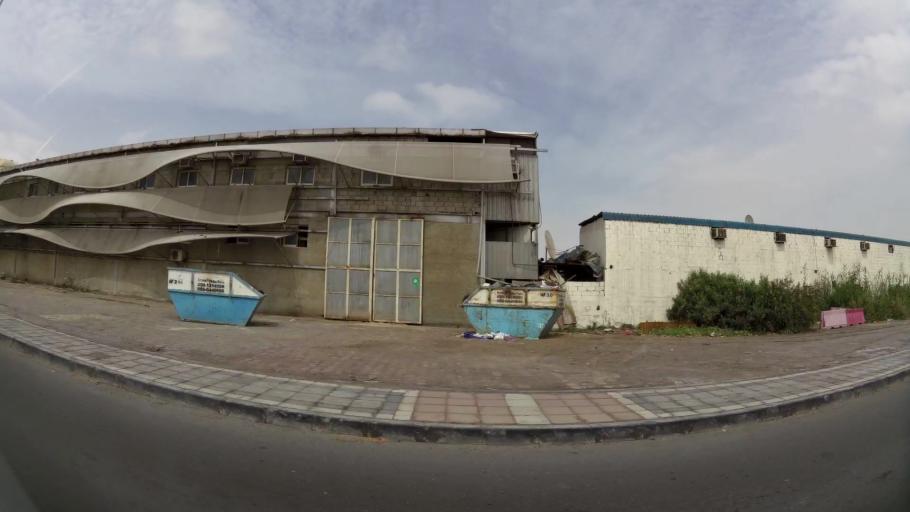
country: AE
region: Abu Dhabi
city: Abu Dhabi
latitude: 24.3681
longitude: 54.4940
